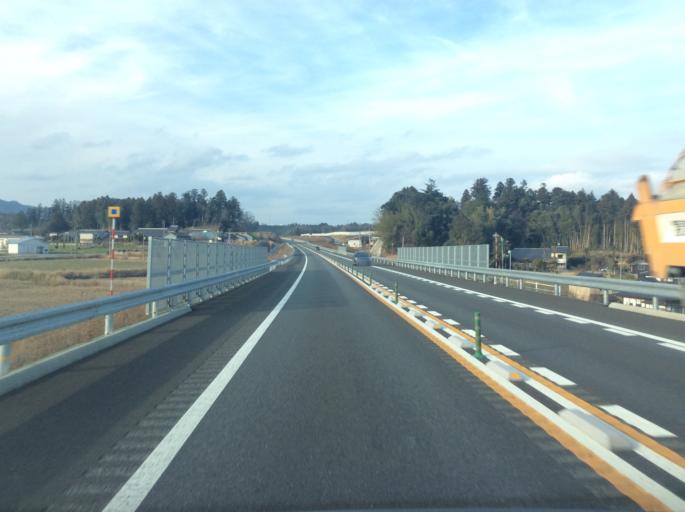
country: JP
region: Fukushima
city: Namie
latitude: 37.5729
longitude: 140.9424
